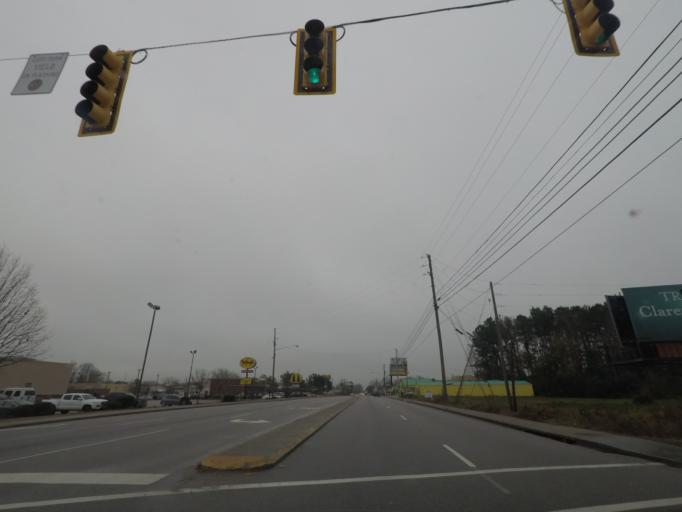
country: US
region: South Carolina
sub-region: Clarendon County
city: Manning
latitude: 33.6977
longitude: -80.2275
